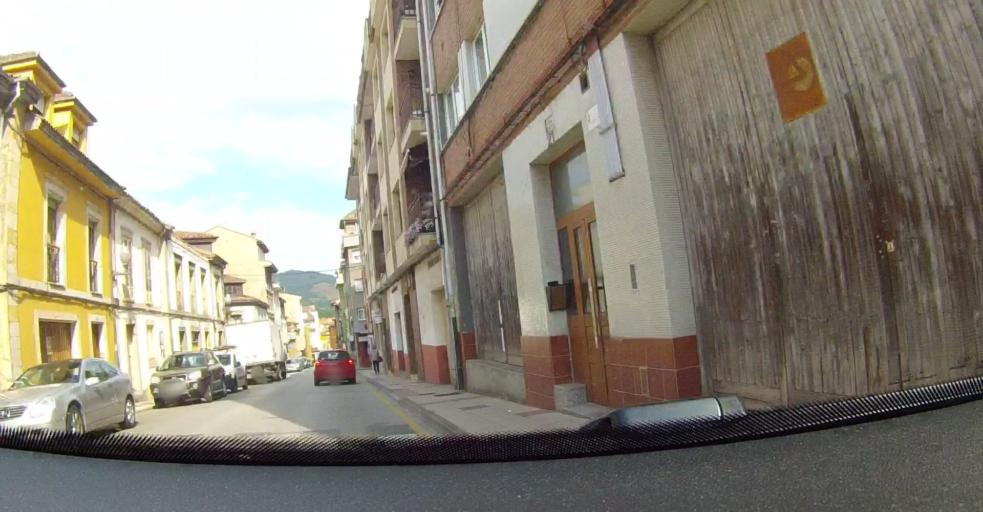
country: ES
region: Asturias
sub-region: Province of Asturias
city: Villaviciosa
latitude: 43.4793
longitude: -5.4332
